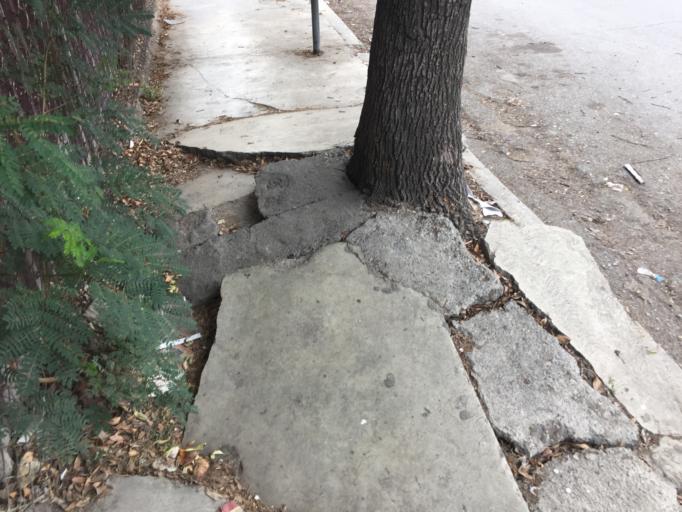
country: MX
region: Nuevo Leon
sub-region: Monterrey
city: Monterrey
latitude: 25.6805
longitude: -100.3041
